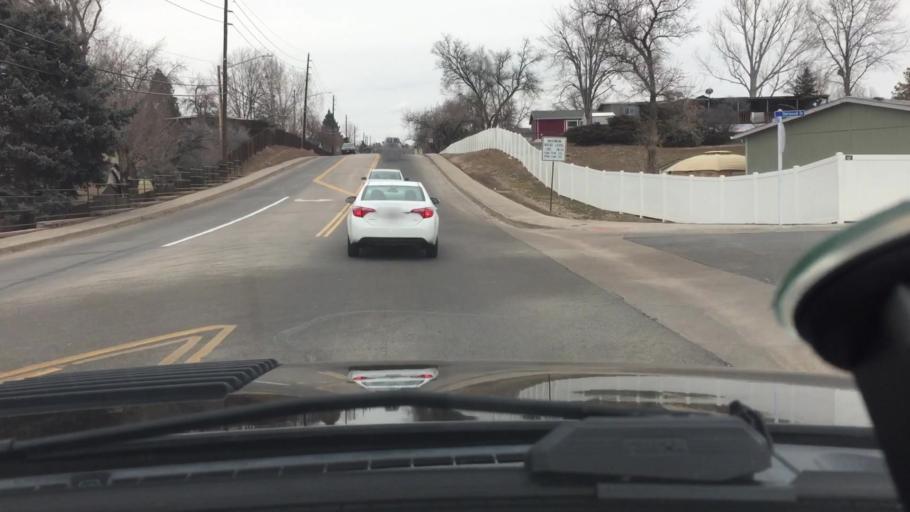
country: US
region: Colorado
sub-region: Adams County
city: Federal Heights
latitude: 39.8648
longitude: -105.0060
